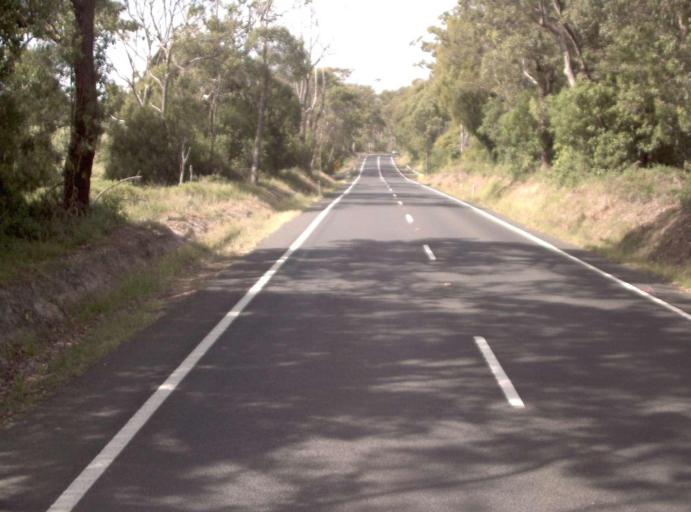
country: AU
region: Victoria
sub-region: East Gippsland
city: Lakes Entrance
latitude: -37.8583
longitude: 148.0296
